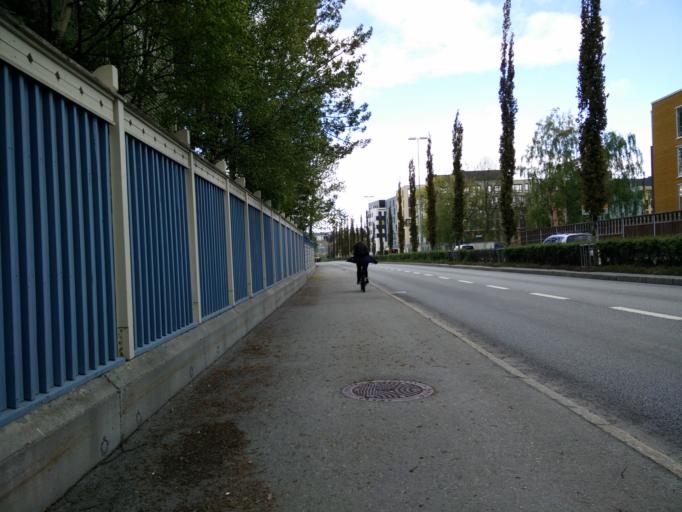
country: NO
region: Sor-Trondelag
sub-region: Trondheim
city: Trondheim
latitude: 63.4102
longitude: 10.3989
